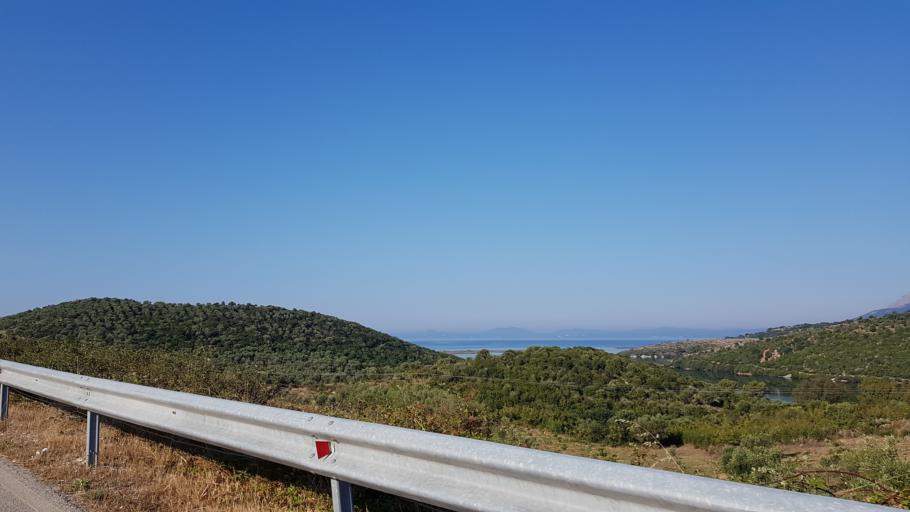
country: AL
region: Vlore
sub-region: Rrethi i Sarandes
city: Xarre
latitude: 39.7537
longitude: 20.0035
